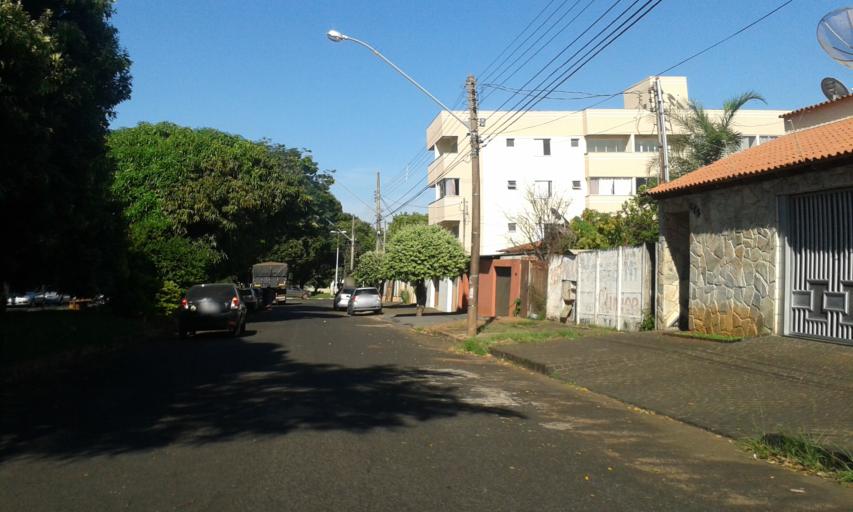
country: BR
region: Minas Gerais
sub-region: Uberlandia
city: Uberlandia
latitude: -18.9003
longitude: -48.2500
